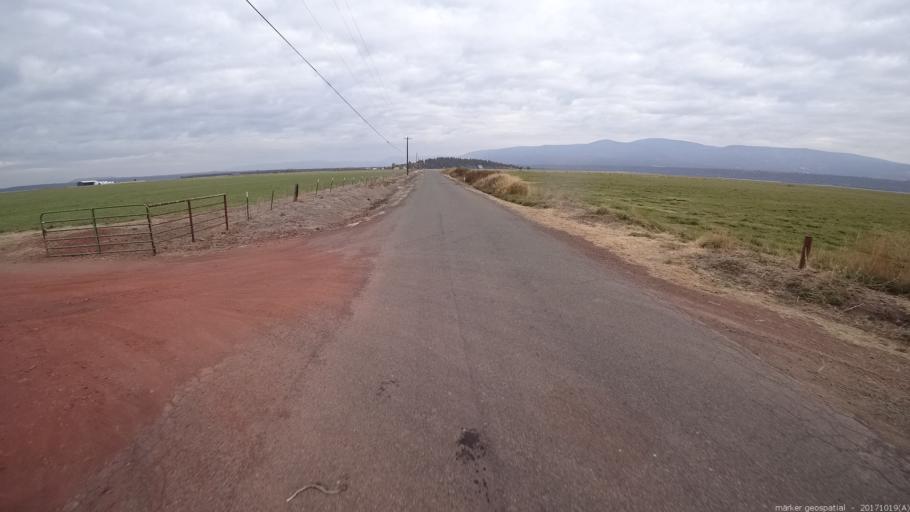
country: US
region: California
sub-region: Shasta County
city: Burney
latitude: 41.0804
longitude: -121.3652
